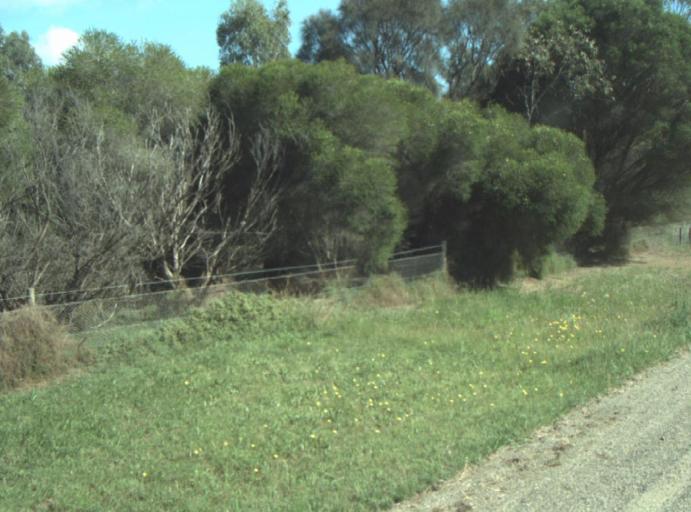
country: AU
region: Victoria
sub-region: Greater Geelong
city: Lara
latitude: -37.9998
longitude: 144.4193
